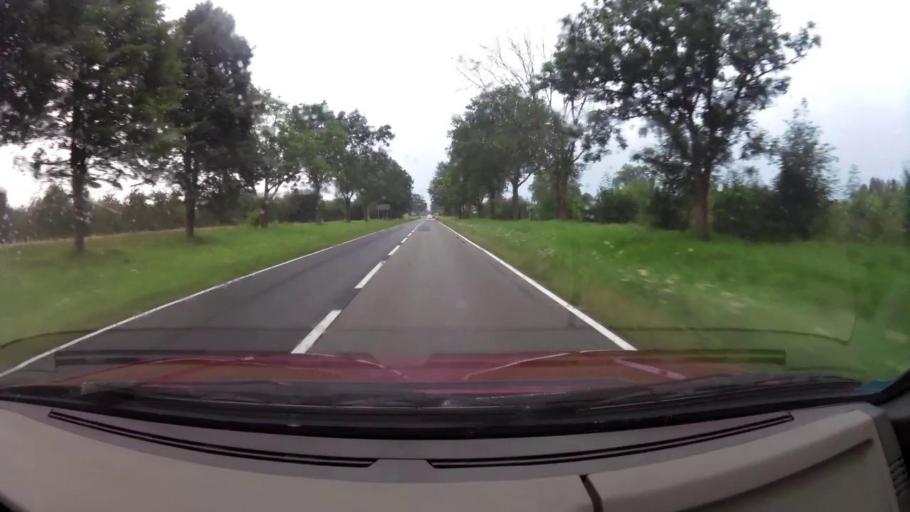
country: PL
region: West Pomeranian Voivodeship
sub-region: Powiat stargardzki
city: Stara Dabrowa
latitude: 53.3856
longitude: 15.1795
